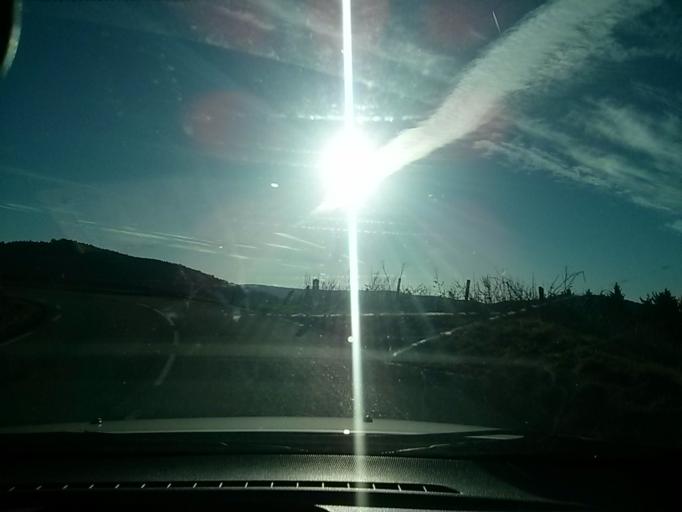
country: FR
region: Rhone-Alpes
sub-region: Departement de la Loire
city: Saint-Genest-Malifaux
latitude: 45.3861
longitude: 4.4550
